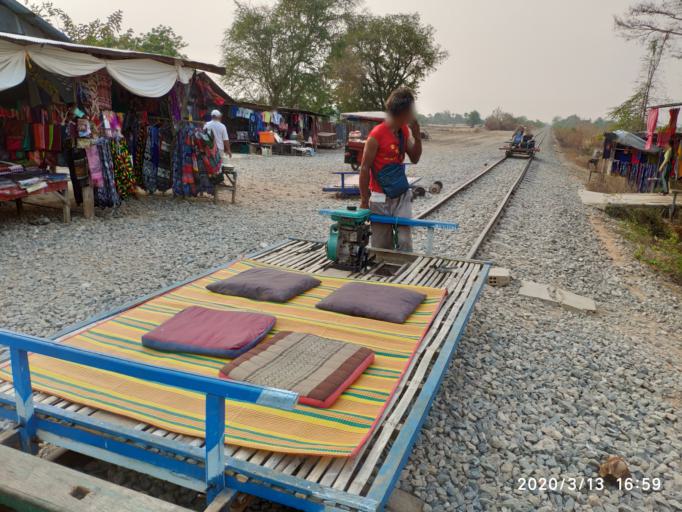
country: KH
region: Battambang
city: Battambang
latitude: 13.0203
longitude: 103.2426
